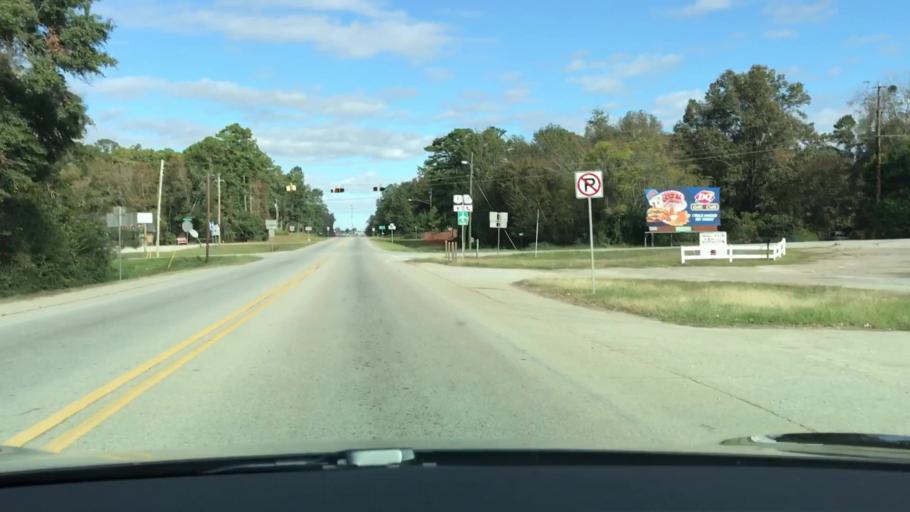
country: US
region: Georgia
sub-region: Jefferson County
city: Louisville
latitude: 32.9958
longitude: -82.3942
